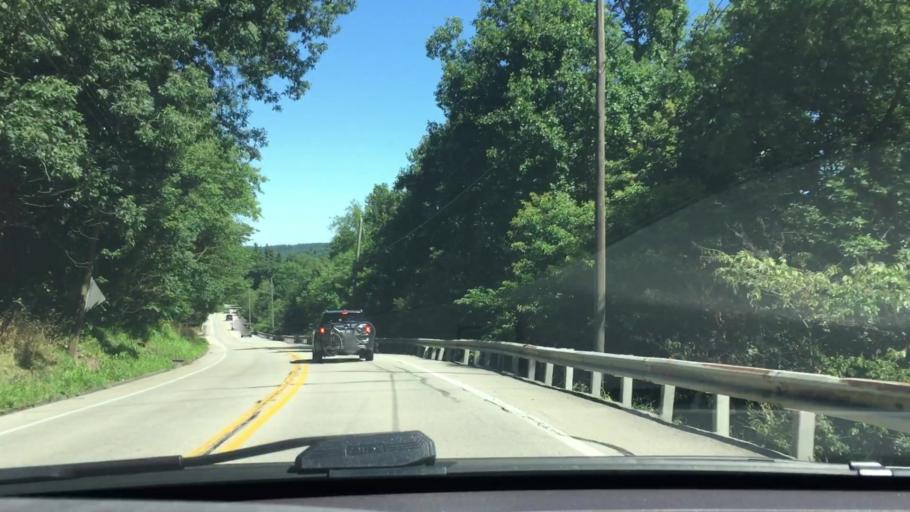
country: US
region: Pennsylvania
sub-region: Westmoreland County
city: West Leechburg
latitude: 40.6254
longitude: -79.6450
